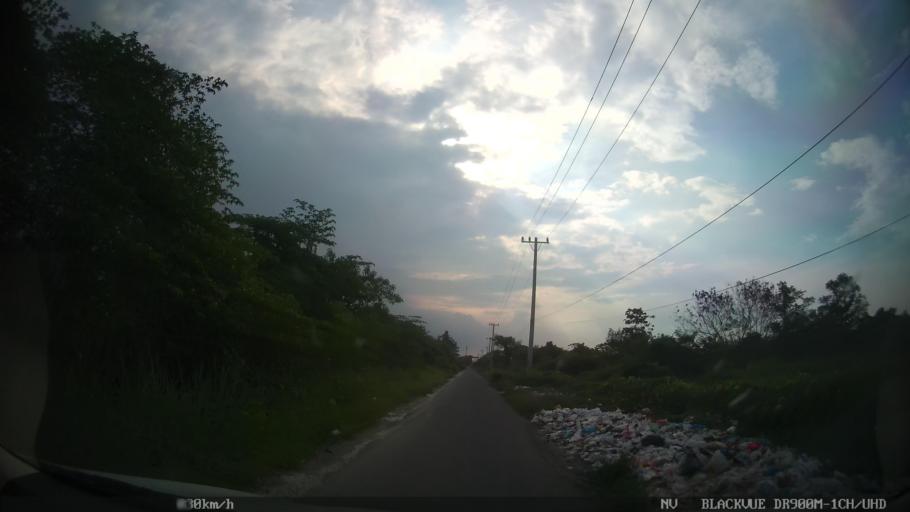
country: ID
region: North Sumatra
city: Medan
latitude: 3.6054
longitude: 98.7336
